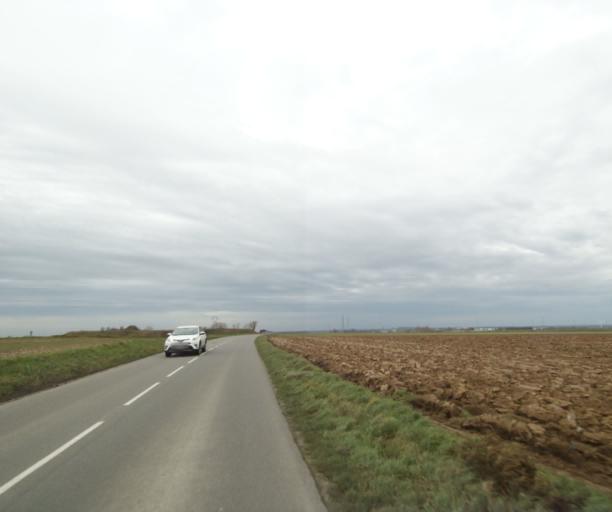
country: FR
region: Nord-Pas-de-Calais
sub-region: Departement du Nord
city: Sebourg
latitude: 50.3531
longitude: 3.6212
